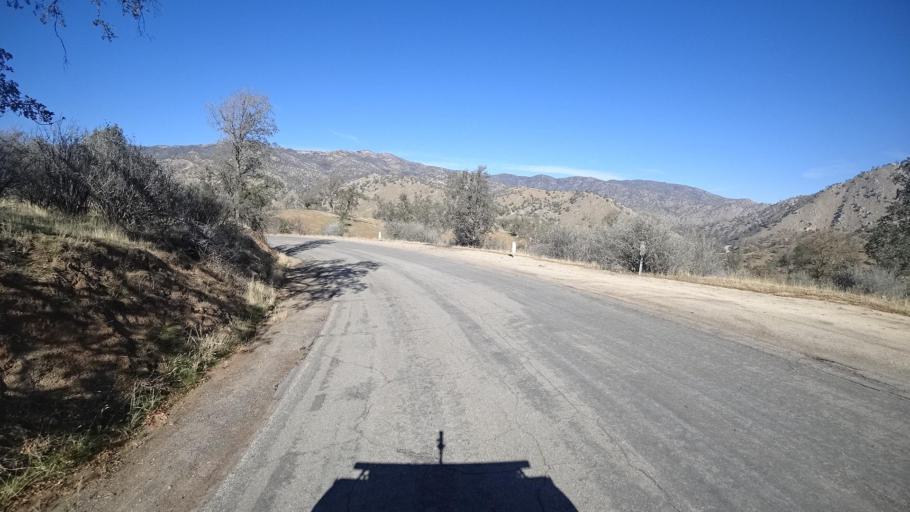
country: US
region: California
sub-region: Kern County
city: Bodfish
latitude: 35.5344
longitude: -118.6305
